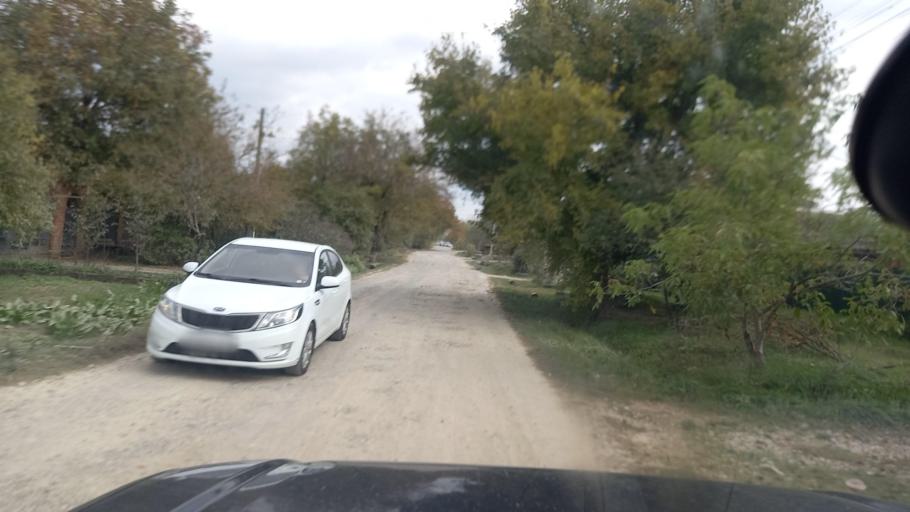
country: RU
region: Krasnodarskiy
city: Il'skiy
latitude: 44.8481
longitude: 38.5566
